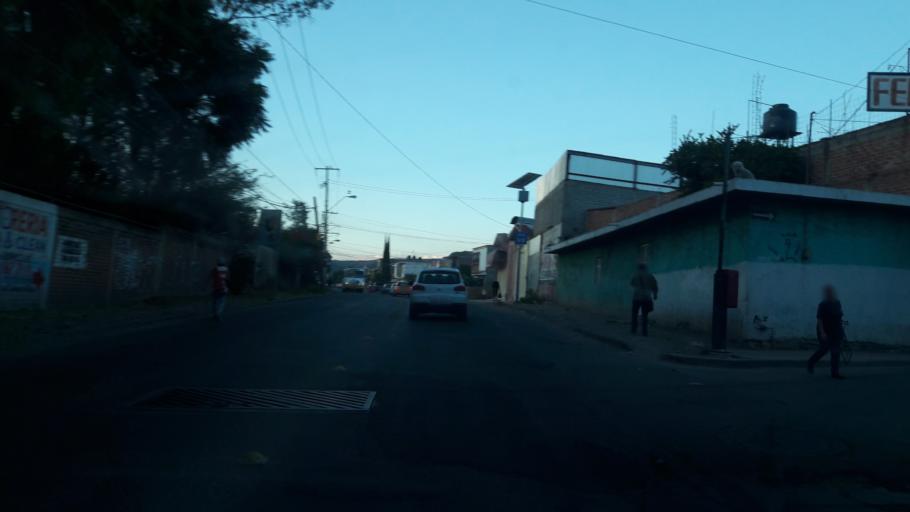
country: MX
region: Guanajuato
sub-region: Leon
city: Medina
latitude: 21.1544
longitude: -101.6342
